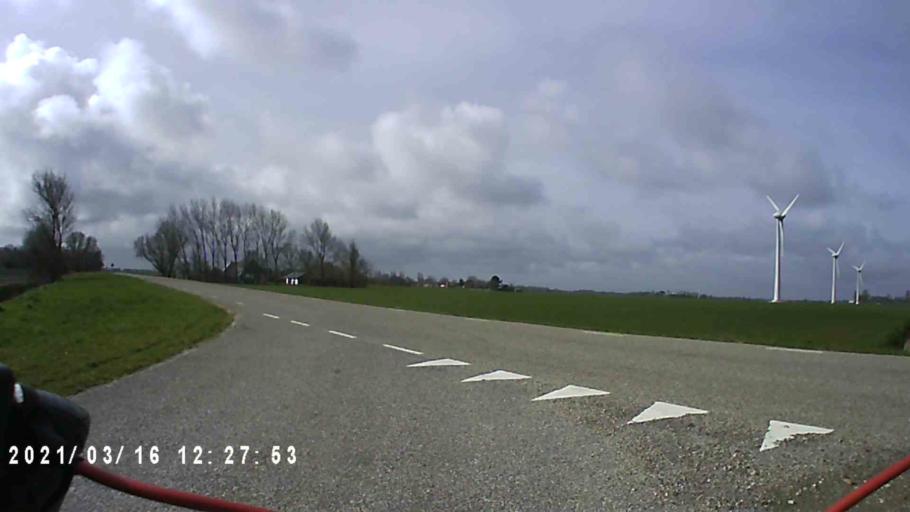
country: NL
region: Friesland
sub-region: Gemeente Leeuwarderadeel
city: Stiens
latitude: 53.2965
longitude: 5.7386
